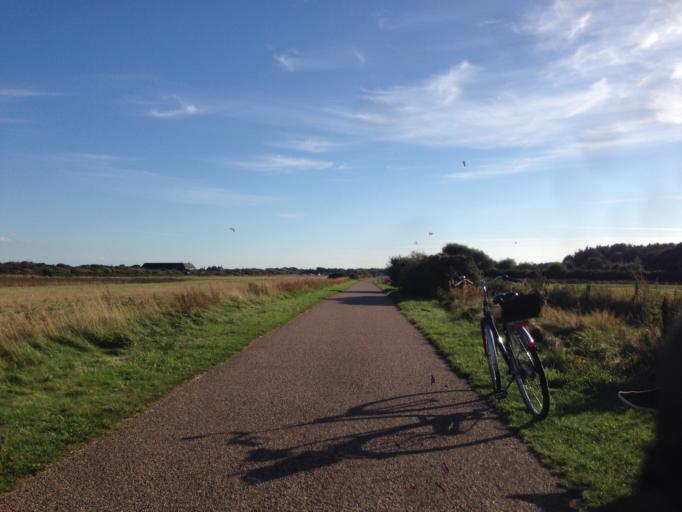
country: DE
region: Schleswig-Holstein
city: Tinnum
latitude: 54.9469
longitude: 8.3351
